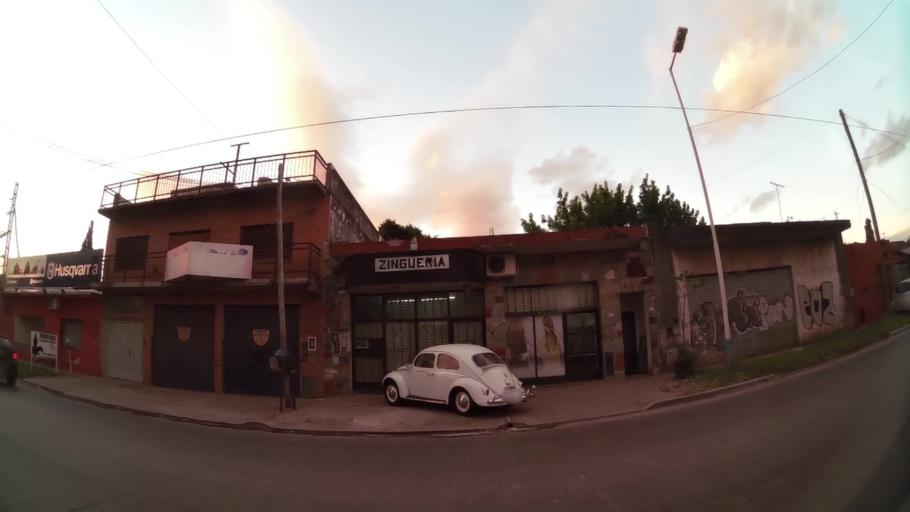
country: AR
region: Buenos Aires
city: Santa Catalina - Dique Lujan
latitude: -34.4730
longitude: -58.7633
